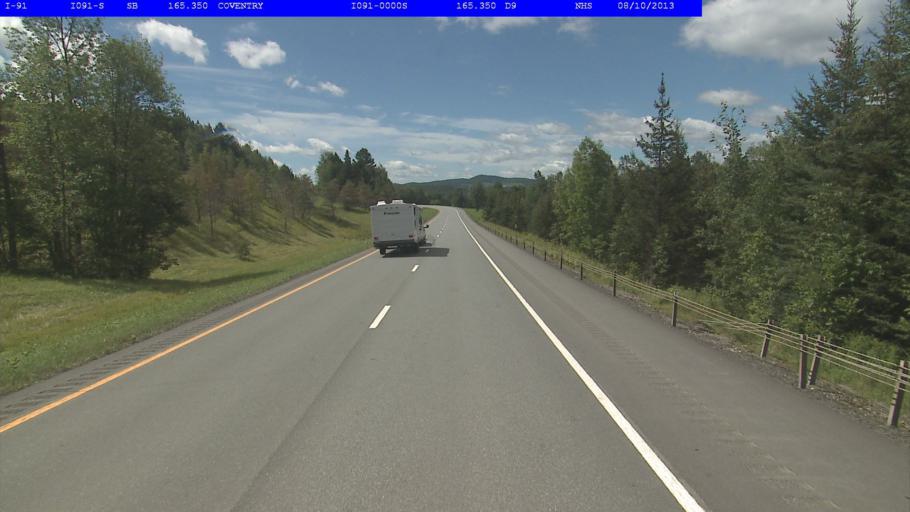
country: US
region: Vermont
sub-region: Orleans County
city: Newport
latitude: 44.8595
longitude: -72.1905
